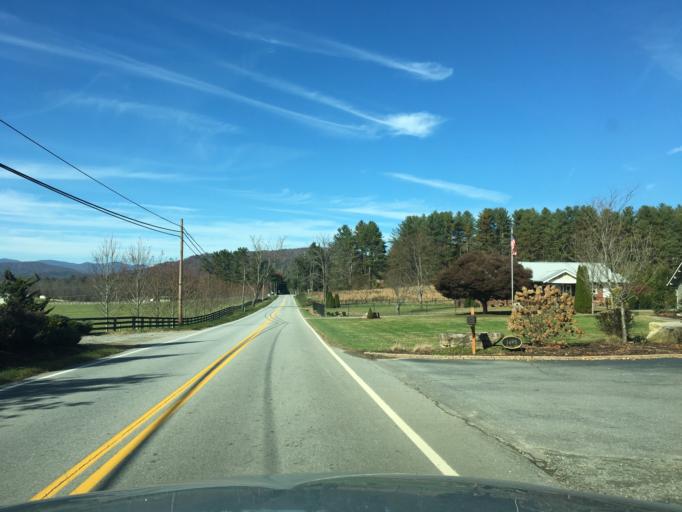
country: US
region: North Carolina
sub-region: Henderson County
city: Etowah
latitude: 35.2515
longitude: -82.6328
